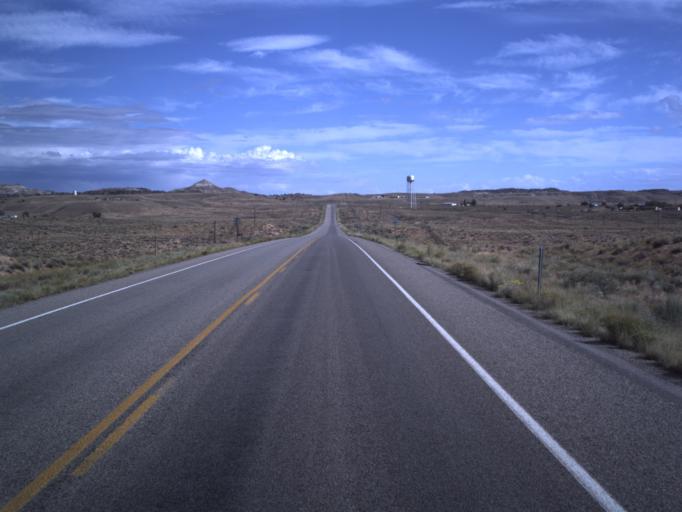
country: US
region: Colorado
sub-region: Montezuma County
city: Towaoc
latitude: 37.2060
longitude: -109.1629
